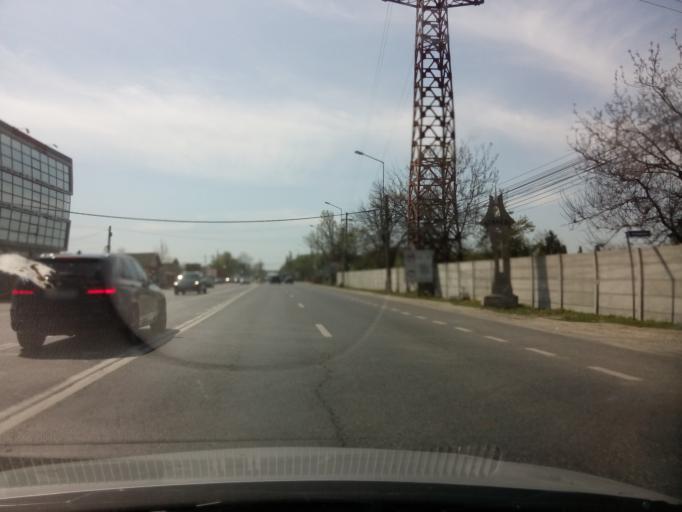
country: RO
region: Ilfov
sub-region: Comuna Corbeanca
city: Corbeanca
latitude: 44.5842
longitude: 26.0704
